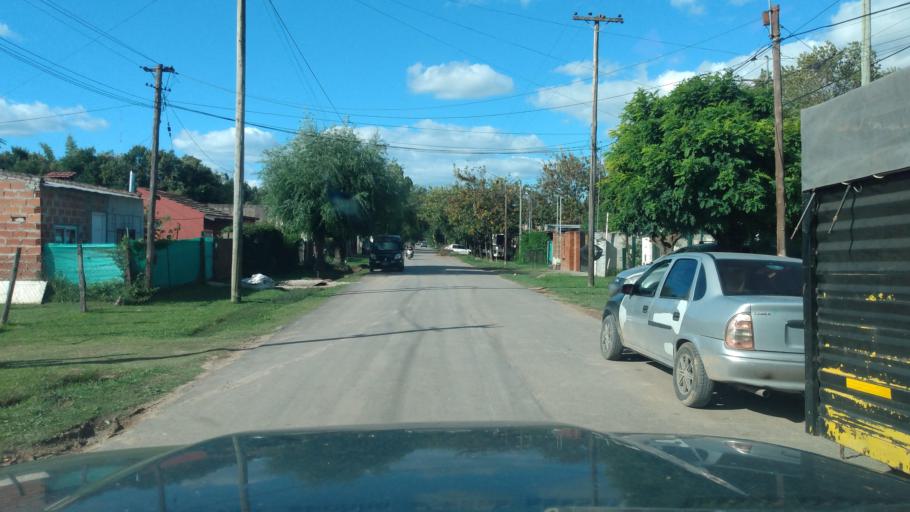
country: AR
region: Buenos Aires
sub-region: Partido de Lujan
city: Lujan
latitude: -34.5813
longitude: -59.0905
